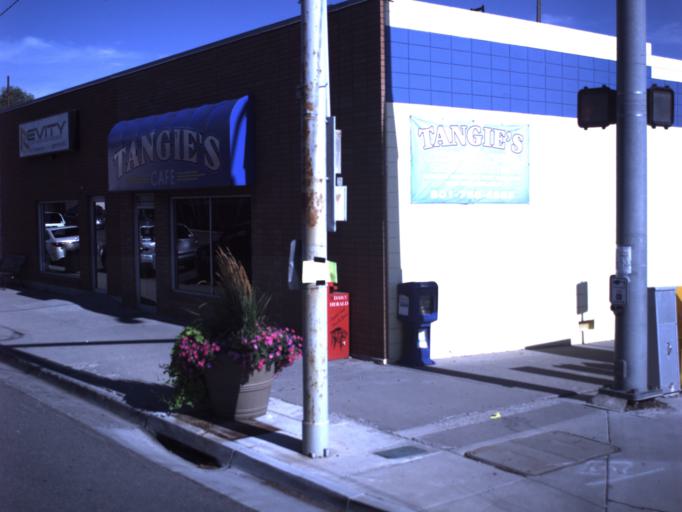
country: US
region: Utah
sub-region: Utah County
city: American Fork
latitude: 40.3767
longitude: -111.7986
